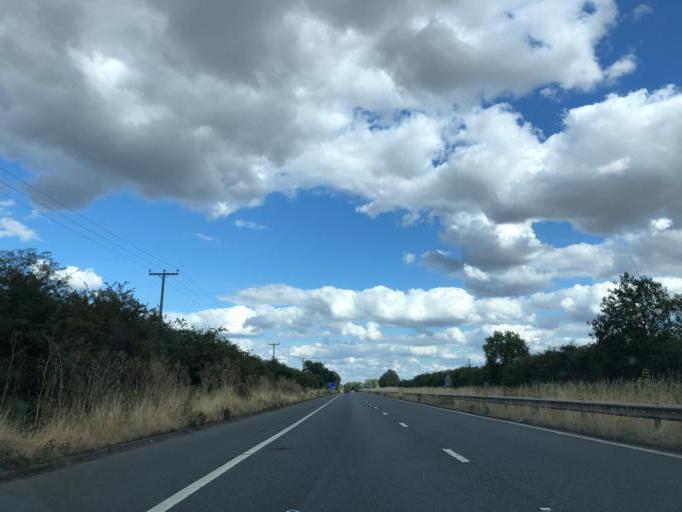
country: GB
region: England
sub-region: Warwickshire
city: Dunchurch
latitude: 52.3385
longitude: -1.3130
